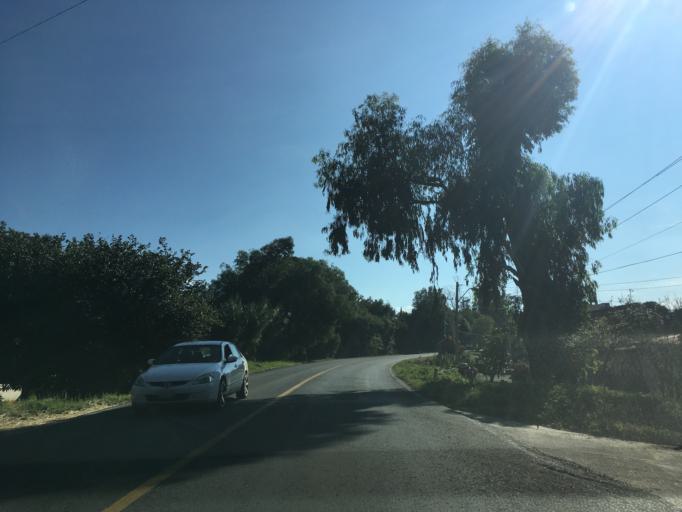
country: MX
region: Mexico
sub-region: Chalco
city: Chilchota
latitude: 19.8507
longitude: -102.1222
